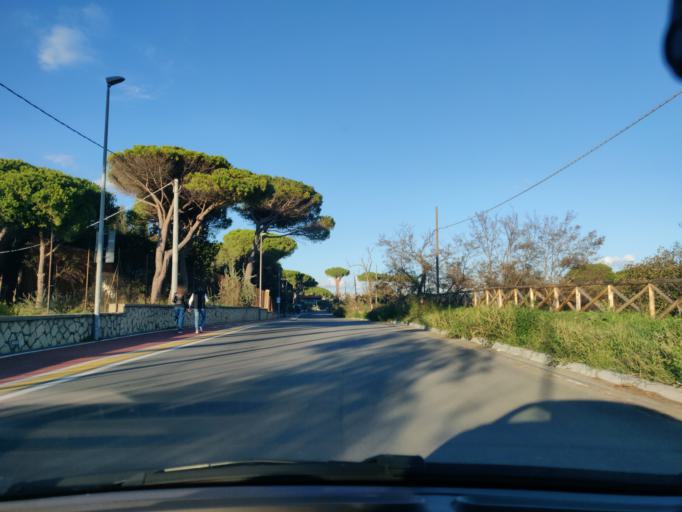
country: IT
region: Latium
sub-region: Provincia di Viterbo
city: Tarquinia
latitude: 42.2148
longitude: 11.7095
